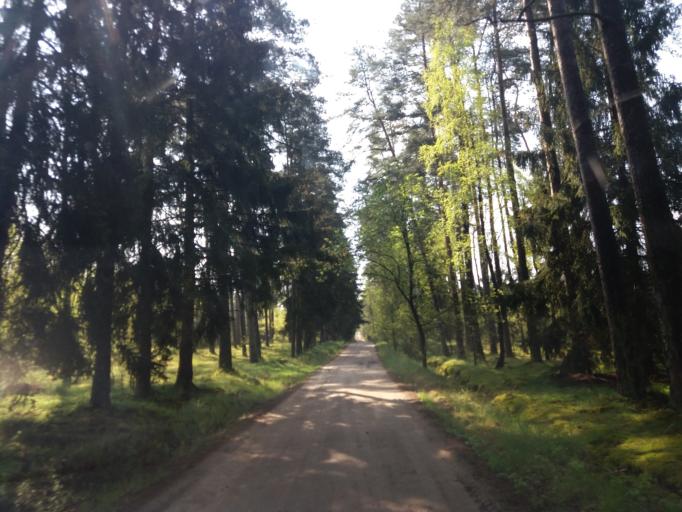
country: PL
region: West Pomeranian Voivodeship
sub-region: Powiat choszczenski
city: Drawno
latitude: 53.2194
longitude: 15.8248
